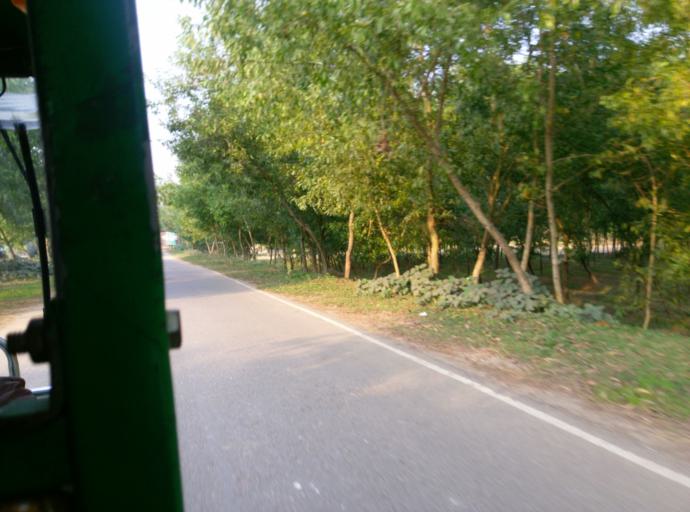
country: BD
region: Dhaka
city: Netrakona
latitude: 25.1469
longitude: 90.6594
